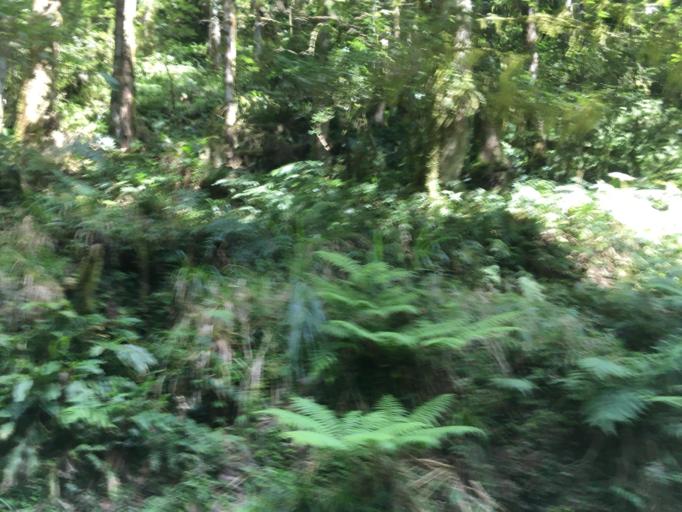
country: TW
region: Taiwan
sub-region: Yilan
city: Yilan
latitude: 24.6214
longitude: 121.4743
